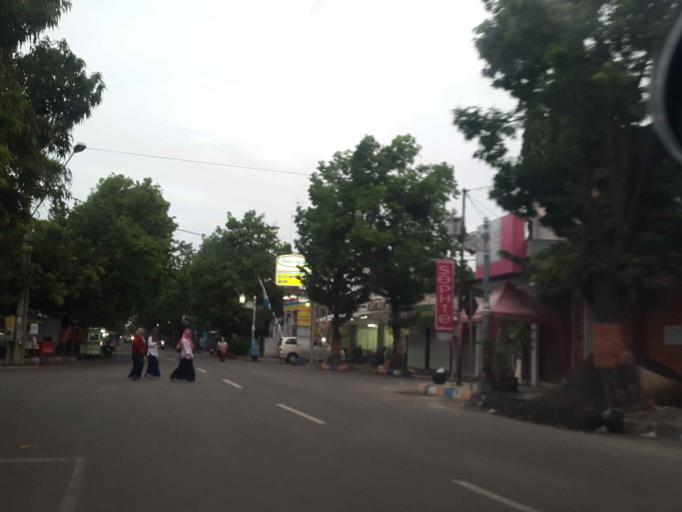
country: ID
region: Central Java
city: Rembangan
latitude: -6.7067
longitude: 111.3420
